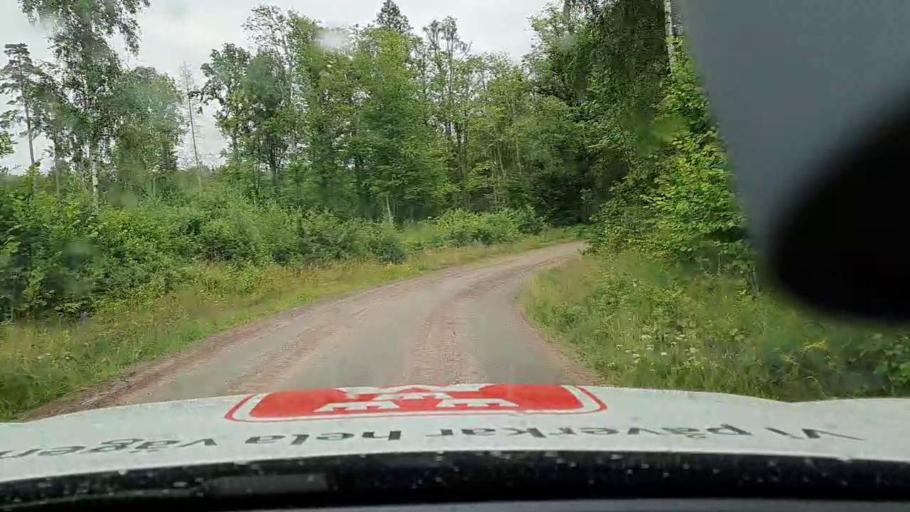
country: SE
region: Vaestra Goetaland
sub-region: Skara Kommun
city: Axvall
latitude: 58.4590
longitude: 13.6611
